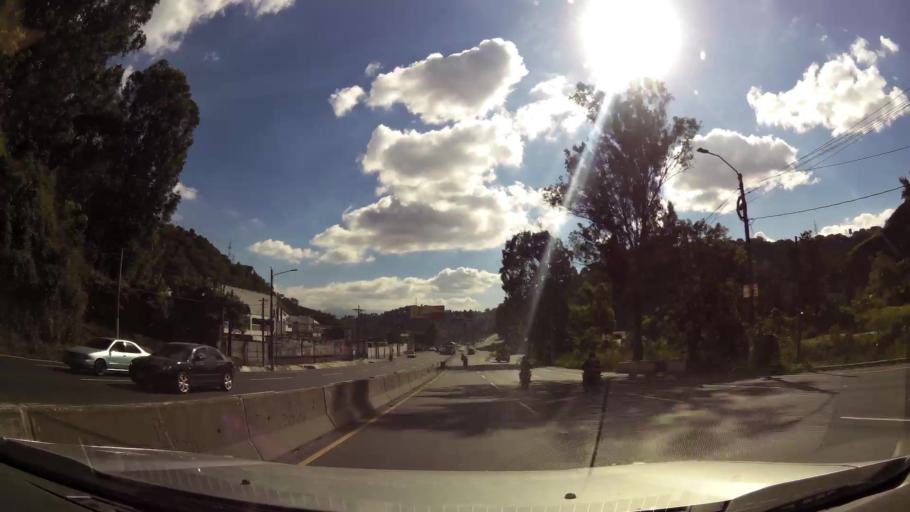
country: GT
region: Guatemala
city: Villa Nueva
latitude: 14.5558
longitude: -90.5765
